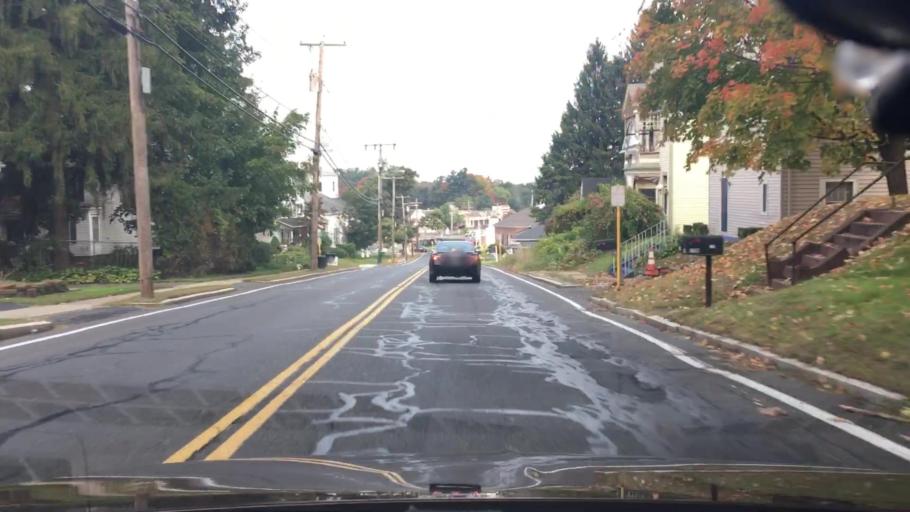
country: US
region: Massachusetts
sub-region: Hampden County
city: East Longmeadow
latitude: 42.0634
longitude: -72.5105
